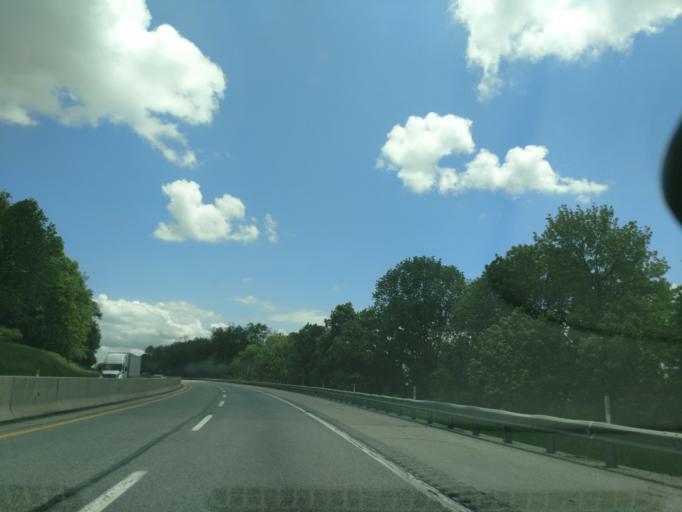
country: US
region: Pennsylvania
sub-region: Lancaster County
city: Denver
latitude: 40.2322
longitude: -76.1269
